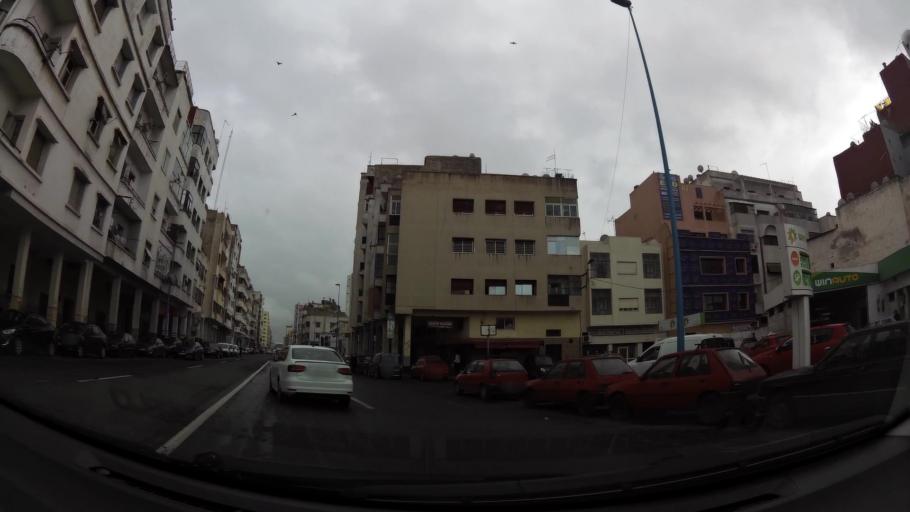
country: MA
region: Grand Casablanca
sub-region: Casablanca
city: Casablanca
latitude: 33.5988
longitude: -7.6311
